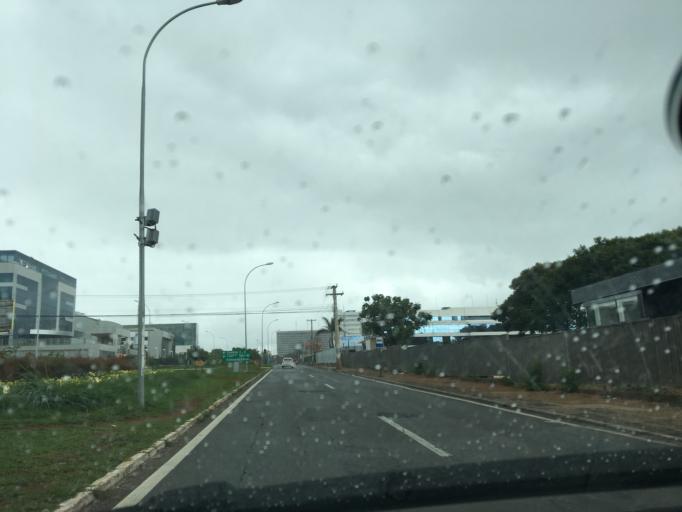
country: BR
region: Federal District
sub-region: Brasilia
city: Brasilia
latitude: -15.7914
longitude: -47.9113
